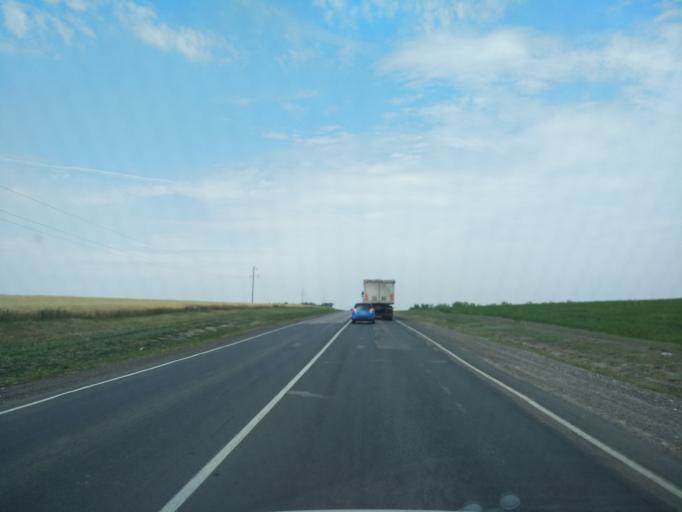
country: RU
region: Voronezj
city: Orlovo
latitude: 51.6825
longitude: 39.5655
